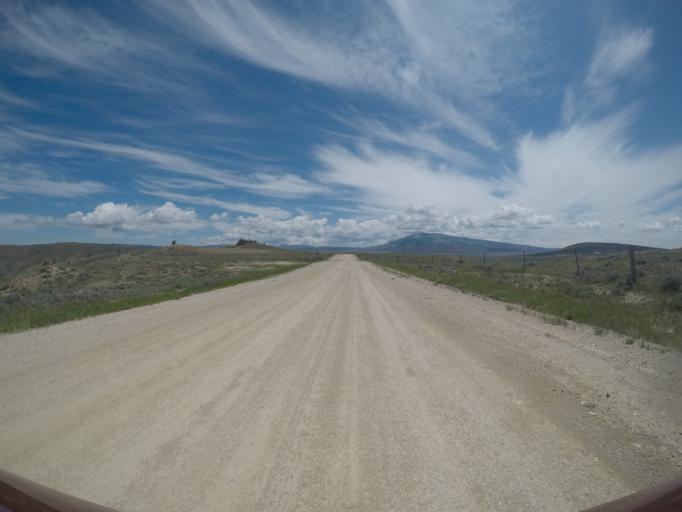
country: US
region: Wyoming
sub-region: Park County
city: Powell
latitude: 45.2065
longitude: -108.7711
